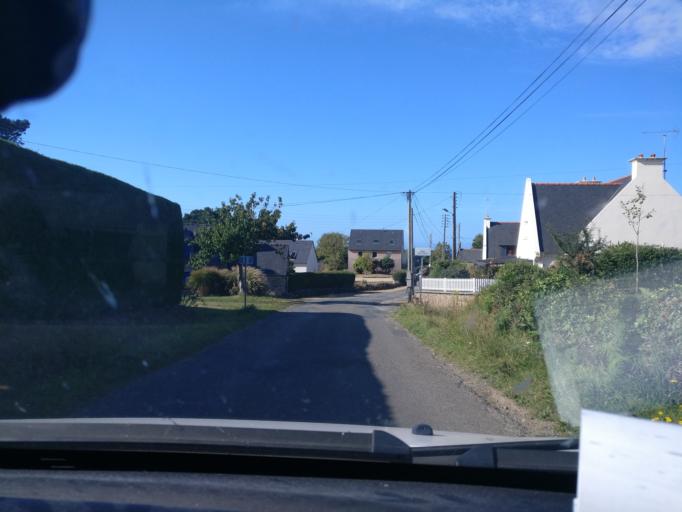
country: FR
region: Brittany
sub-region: Departement des Cotes-d'Armor
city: Trelevern
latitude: 48.8136
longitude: -3.3696
